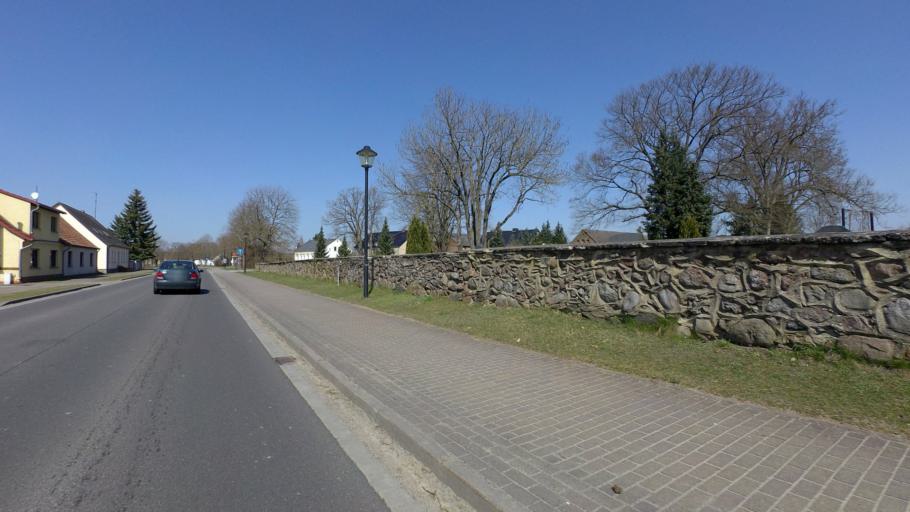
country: DE
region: Brandenburg
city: Ruthnick
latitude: 52.9038
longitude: 12.9688
